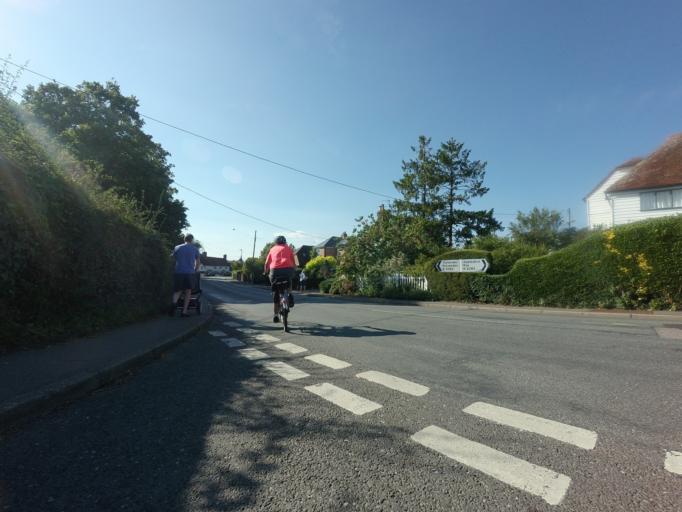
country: GB
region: England
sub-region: Kent
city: Tenterden
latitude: 51.0139
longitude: 0.7078
